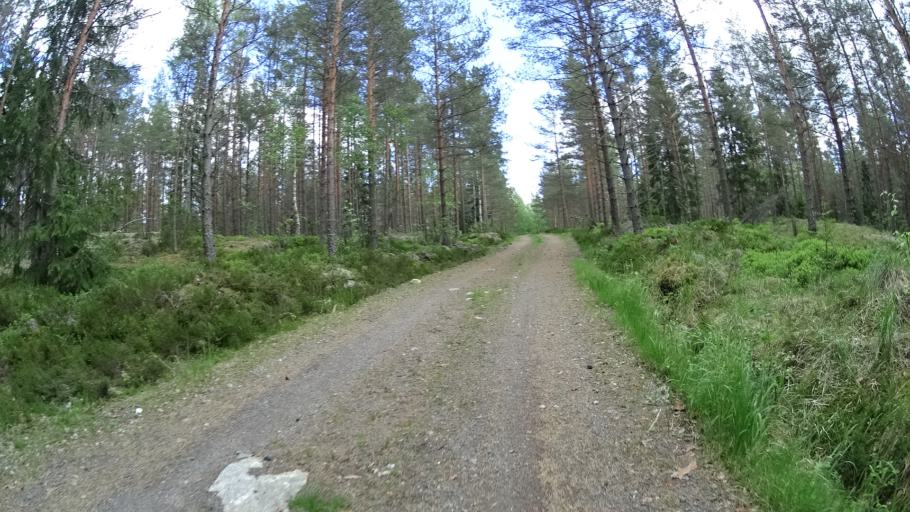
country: FI
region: Varsinais-Suomi
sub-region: Salo
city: Kisko
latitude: 60.1827
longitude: 23.5545
